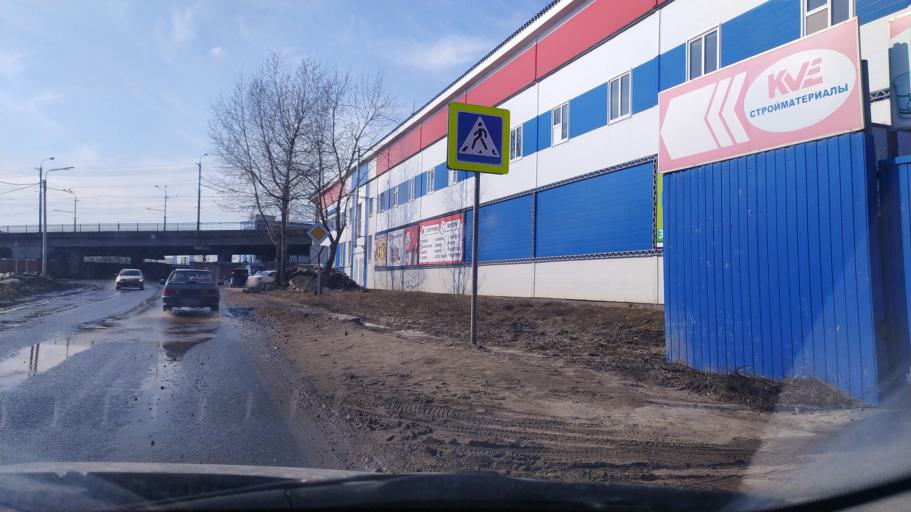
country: RU
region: Chuvashia
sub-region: Cheboksarskiy Rayon
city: Cheboksary
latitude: 56.1178
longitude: 47.2776
